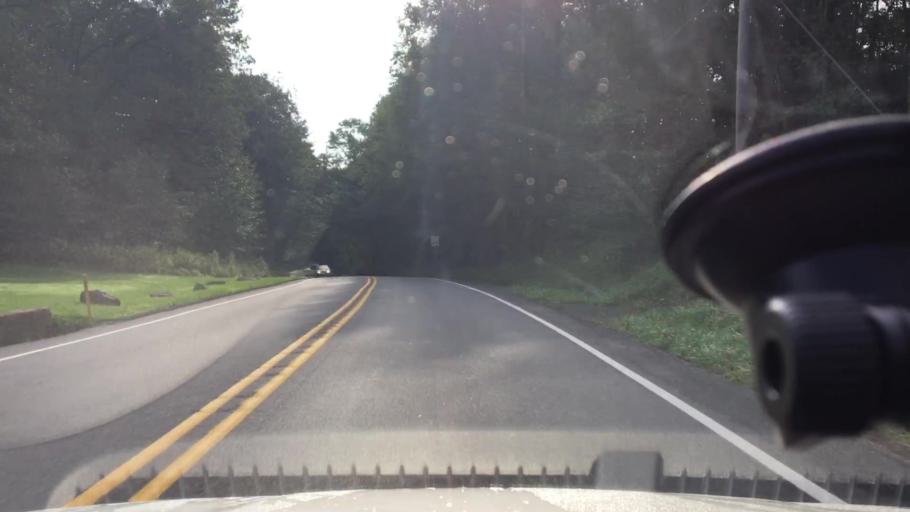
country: US
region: Pennsylvania
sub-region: Monroe County
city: Parkside
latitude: 41.1255
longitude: -75.2923
